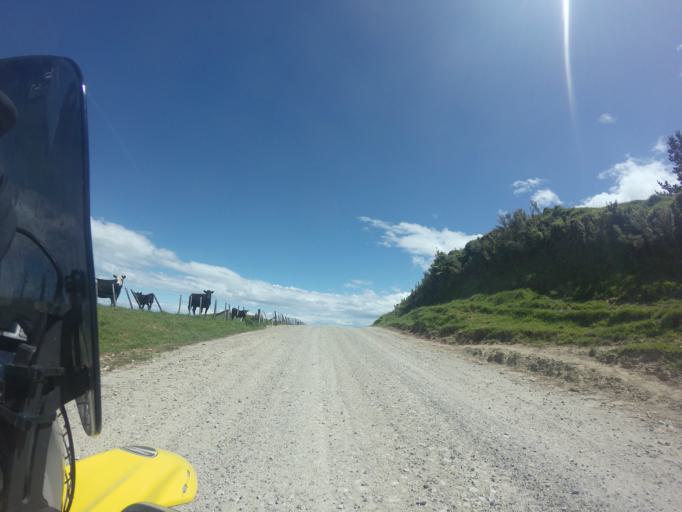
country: NZ
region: Hawke's Bay
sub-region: Wairoa District
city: Wairoa
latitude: -38.9632
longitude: 177.7110
